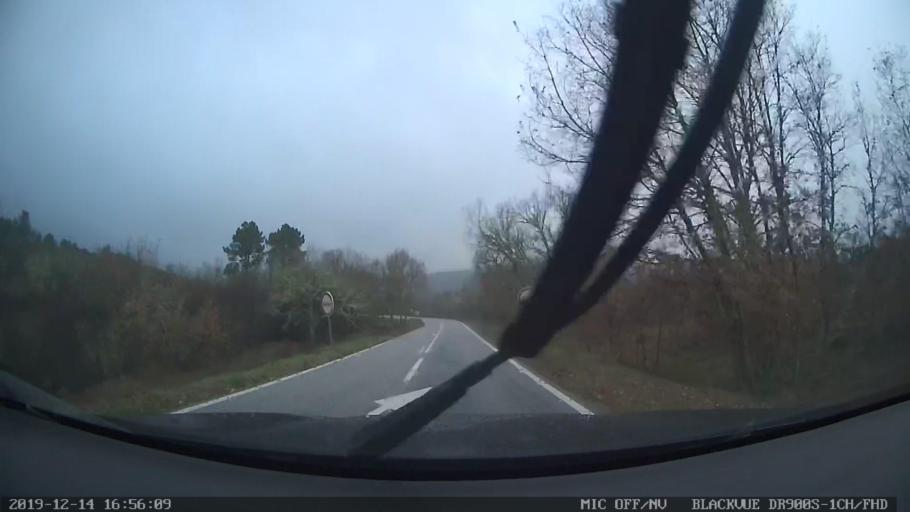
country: PT
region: Vila Real
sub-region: Murca
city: Murca
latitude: 41.4359
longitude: -7.5373
